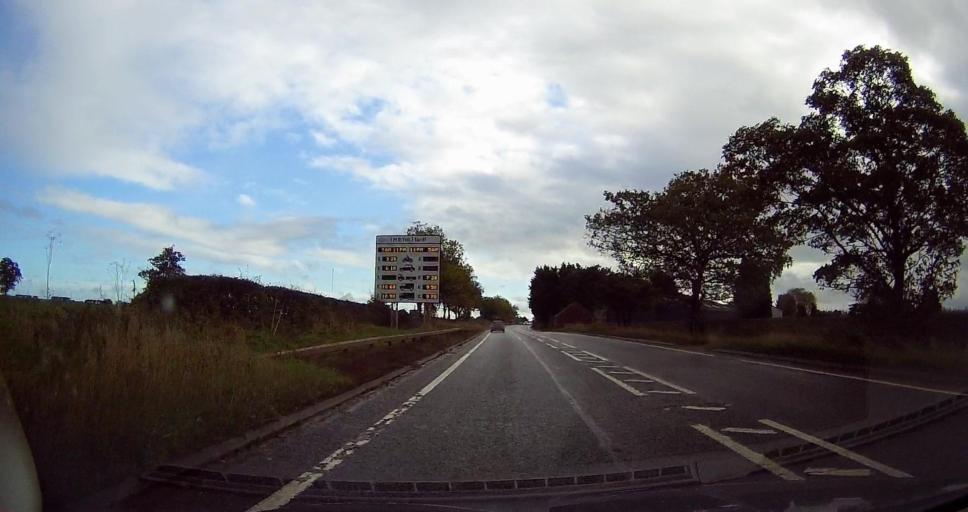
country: GB
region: England
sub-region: Staffordshire
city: Shenstone
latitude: 52.6432
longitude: -1.8142
